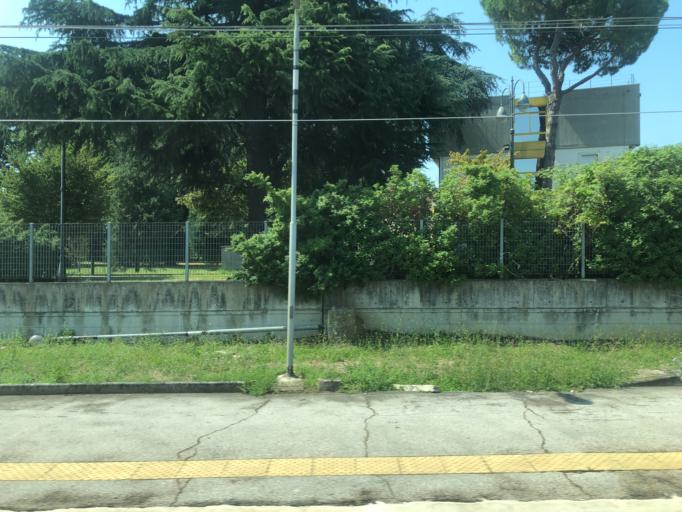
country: IT
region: Emilia-Romagna
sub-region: Forli-Cesena
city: Cesena
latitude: 44.1444
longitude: 12.2528
